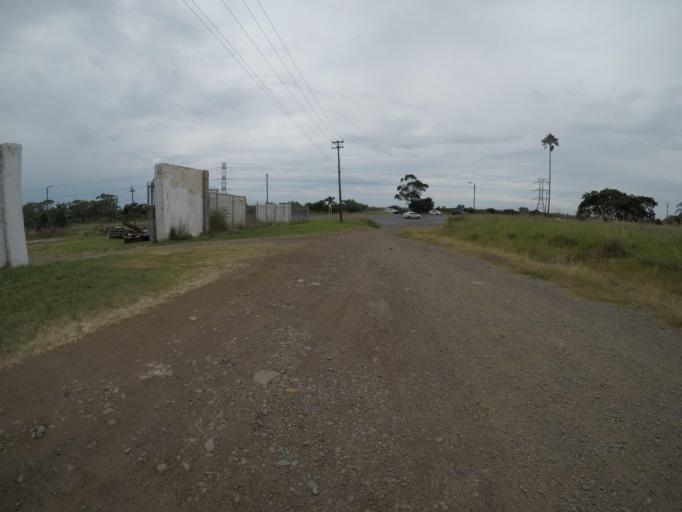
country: ZA
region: Eastern Cape
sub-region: Buffalo City Metropolitan Municipality
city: East London
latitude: -32.9676
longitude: 27.8491
